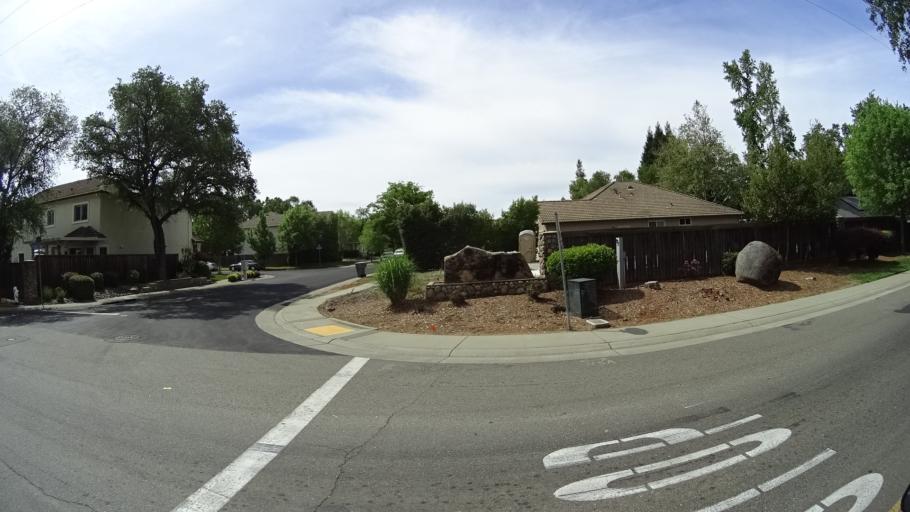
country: US
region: California
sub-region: Placer County
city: Loomis
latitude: 38.8104
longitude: -121.2005
